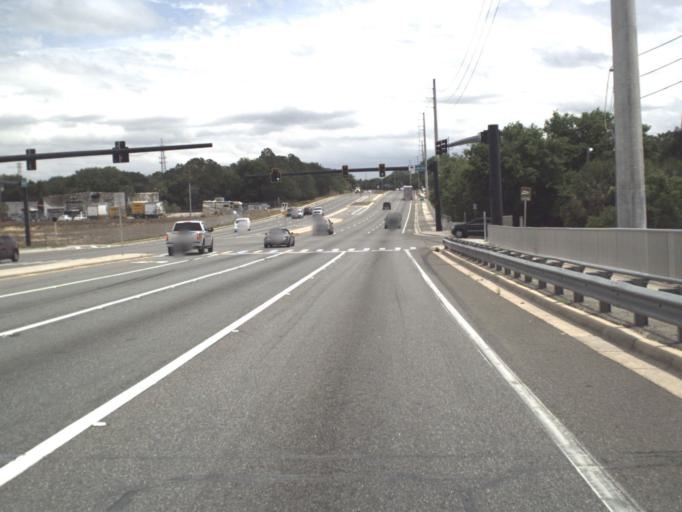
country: US
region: Florida
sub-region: Orange County
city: Oakland
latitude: 28.5463
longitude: -81.6602
